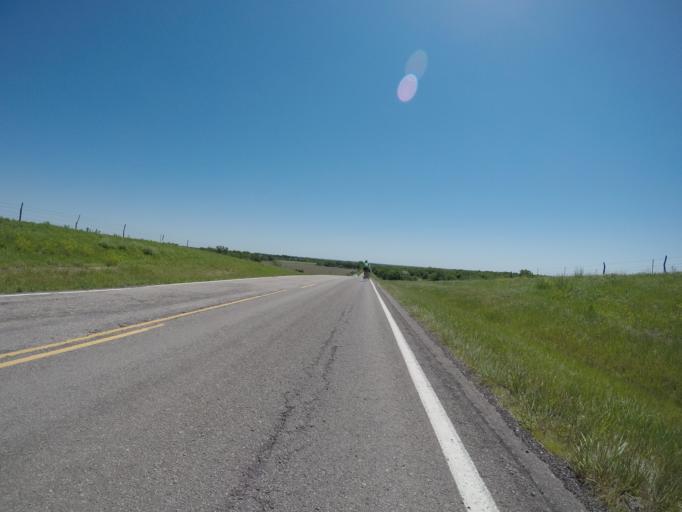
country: US
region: Kansas
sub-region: Shawnee County
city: Auburn
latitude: 38.9065
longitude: -95.9583
